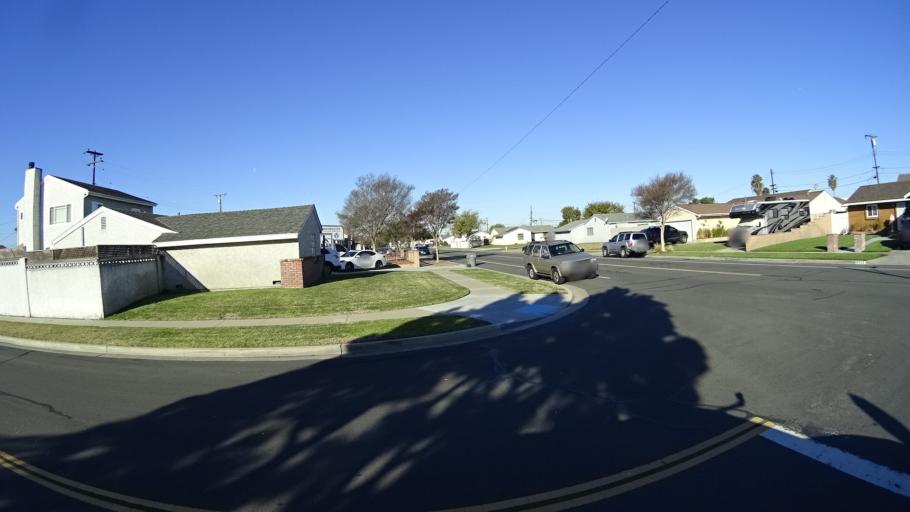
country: US
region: California
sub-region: Orange County
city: Cypress
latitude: 33.8142
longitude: -118.0177
